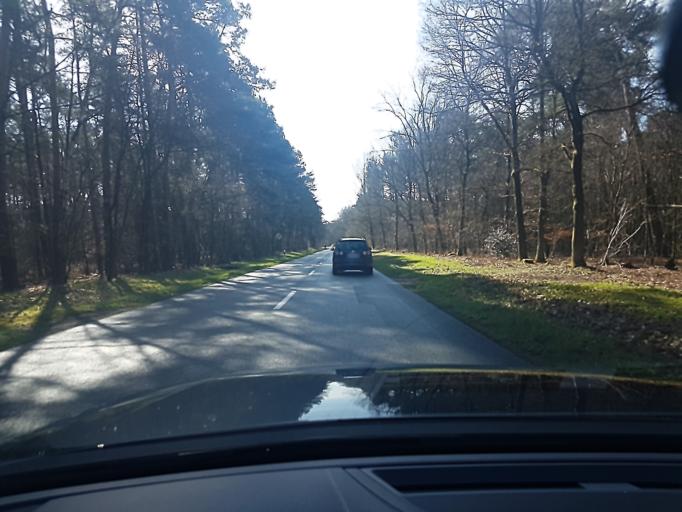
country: DE
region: North Rhine-Westphalia
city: Olfen
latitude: 51.7150
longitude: 7.3098
